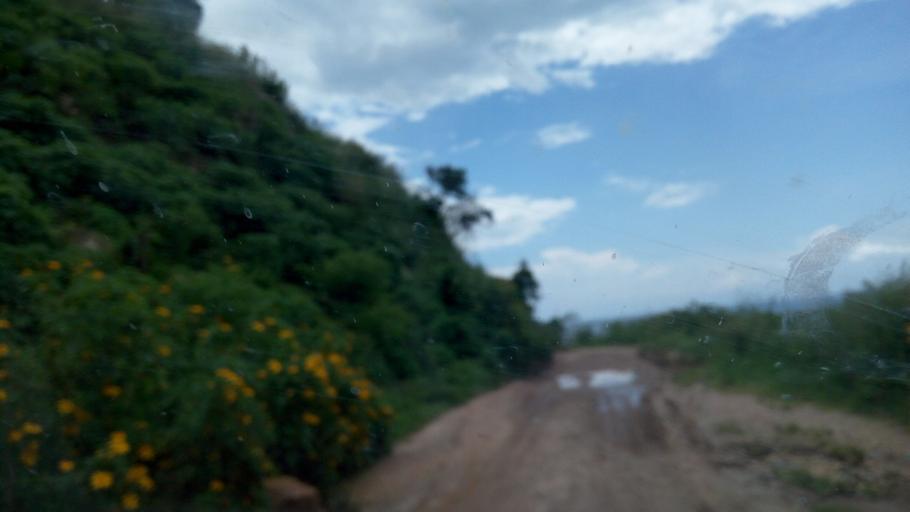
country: CD
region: South Kivu
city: Uvira
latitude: -3.5196
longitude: 29.1494
